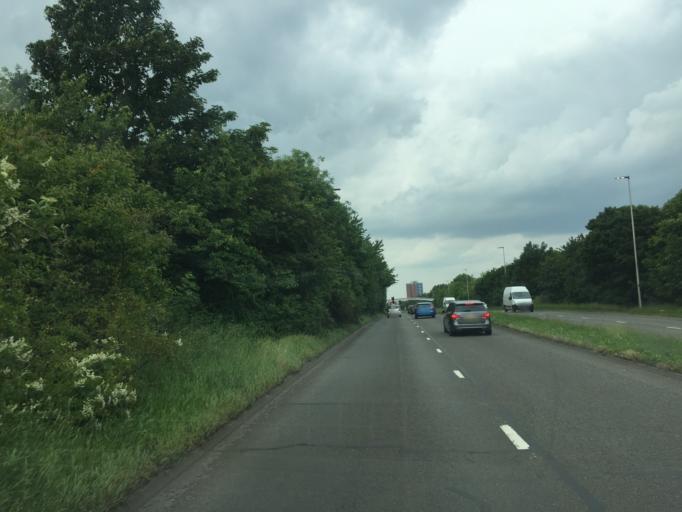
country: GB
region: England
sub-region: Sandwell
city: West Bromwich
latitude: 52.5154
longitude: -1.9815
